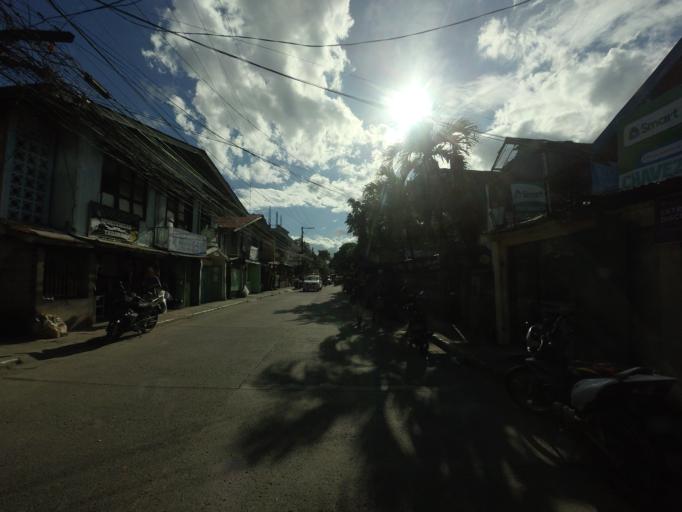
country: PH
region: Central Visayas
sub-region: Province of Negros Oriental
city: Dumaguete
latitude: 9.3060
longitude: 123.3022
